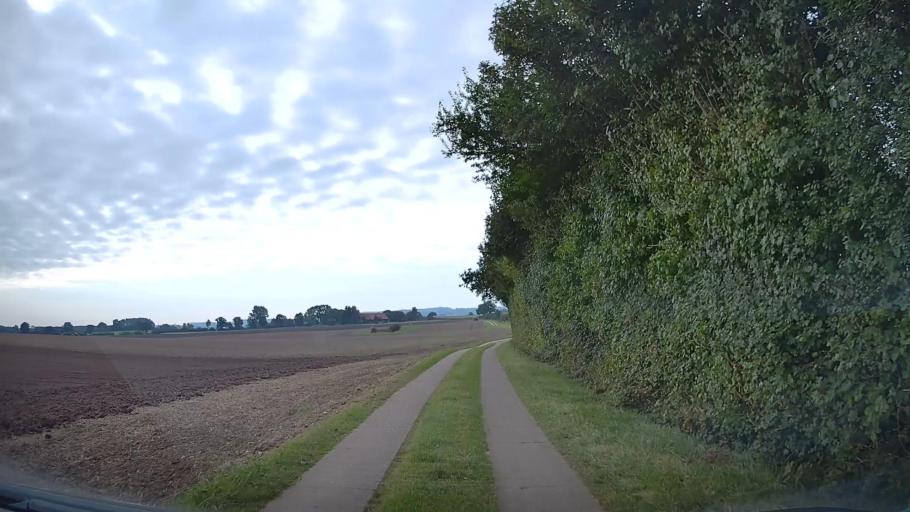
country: DE
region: Schleswig-Holstein
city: Panker
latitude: 54.3651
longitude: 10.5552
